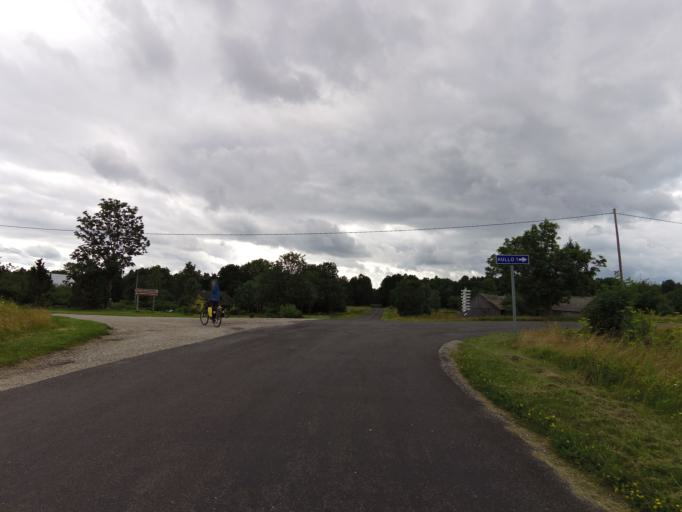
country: EE
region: Laeaene
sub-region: Vormsi vald
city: Hullo
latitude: 58.9880
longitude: 23.2459
